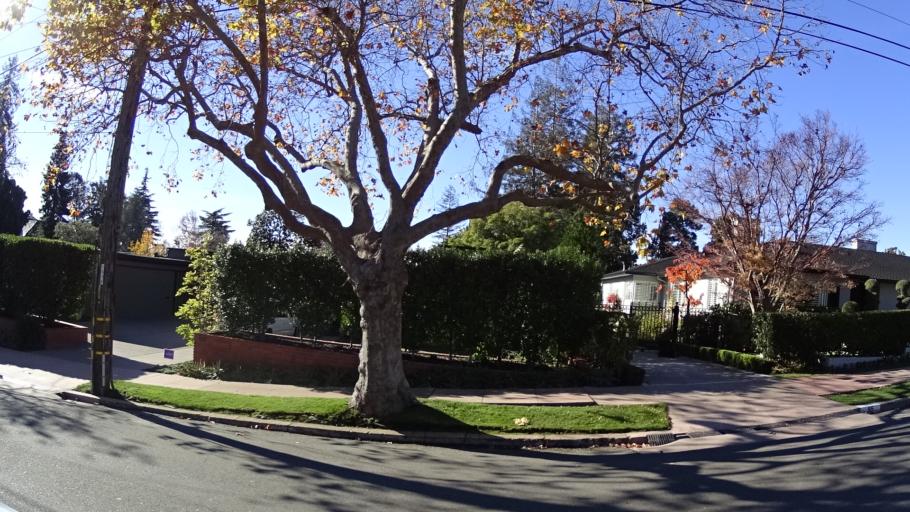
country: US
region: California
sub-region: Alameda County
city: Piedmont
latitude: 37.8182
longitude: -122.2229
